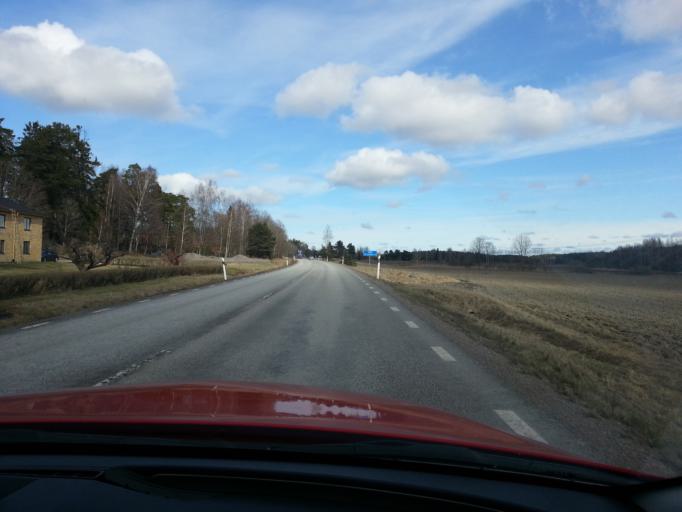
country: SE
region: Uppsala
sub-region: Osthammars Kommun
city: Gimo
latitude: 60.0649
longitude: 18.0852
